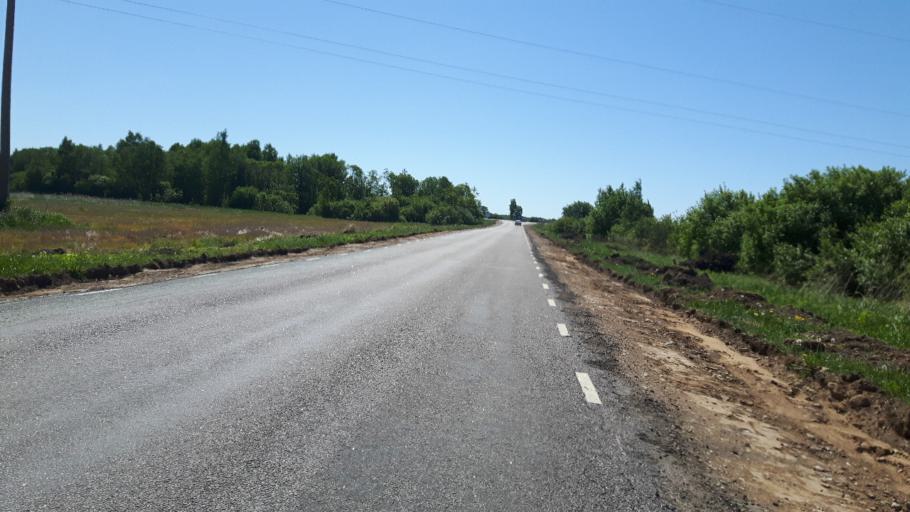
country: EE
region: Ida-Virumaa
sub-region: Narva-Joesuu linn
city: Narva-Joesuu
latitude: 59.3815
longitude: 27.9213
